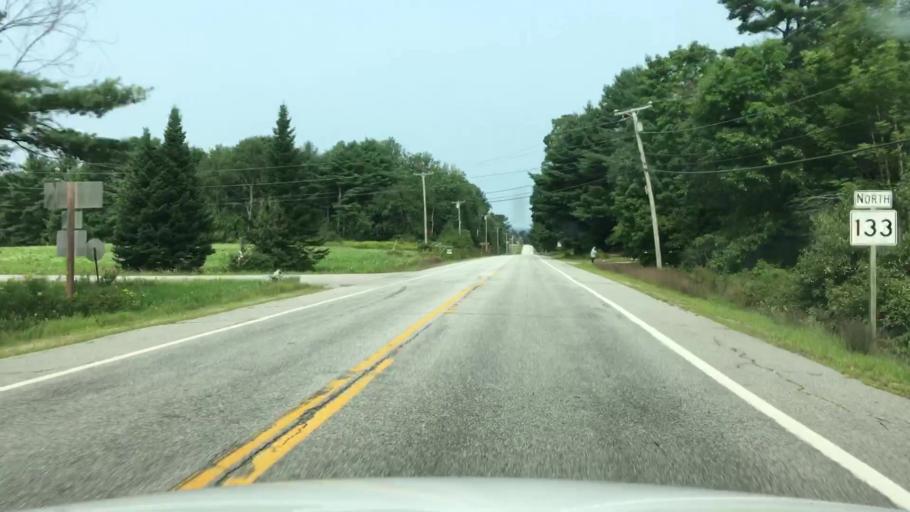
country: US
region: Maine
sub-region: Kennebec County
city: Wayne
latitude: 44.4042
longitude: -70.1309
